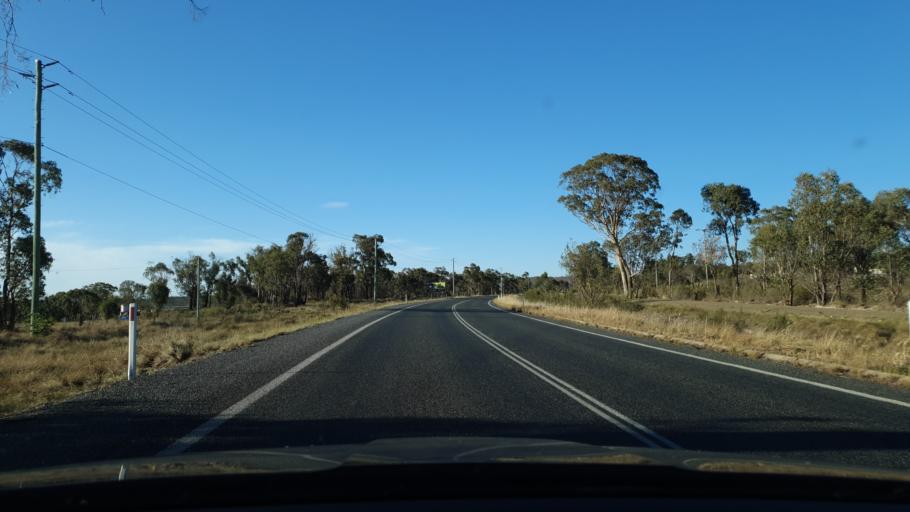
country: AU
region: Queensland
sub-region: Southern Downs
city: Stanthorpe
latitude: -28.6672
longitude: 151.9155
